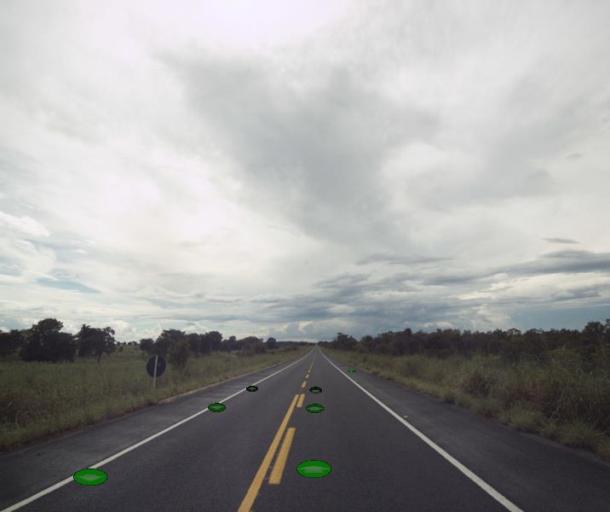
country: BR
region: Goias
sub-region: Sao Miguel Do Araguaia
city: Sao Miguel do Araguaia
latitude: -13.2687
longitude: -50.5088
